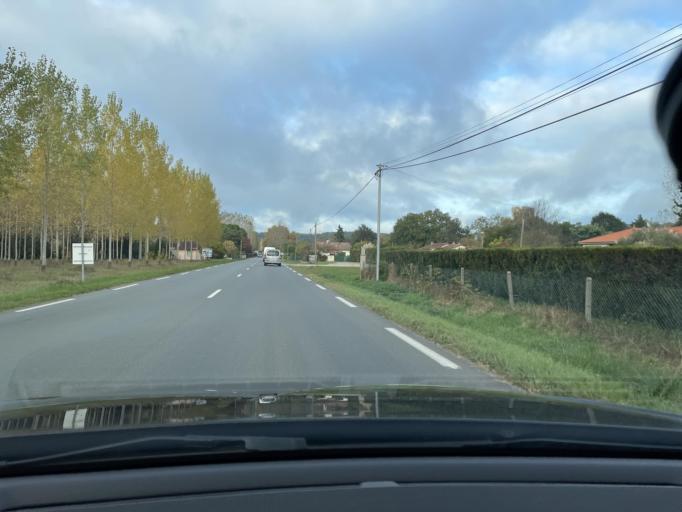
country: FR
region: Aquitaine
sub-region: Departement du Lot-et-Garonne
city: Casteljaloux
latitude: 44.3332
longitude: 0.1009
